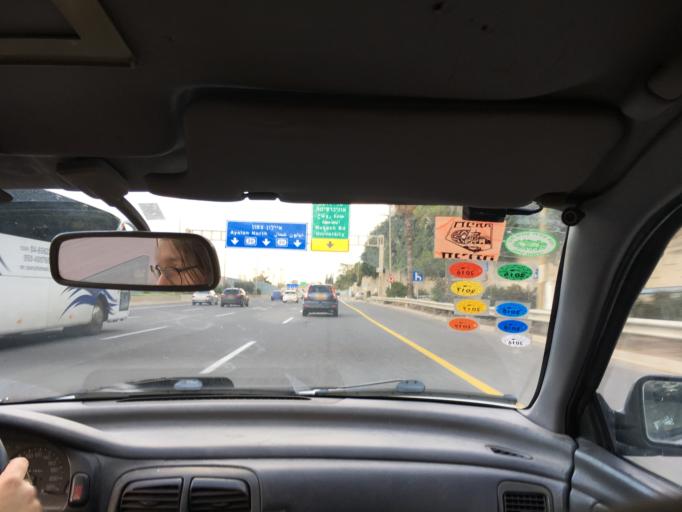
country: IL
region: Tel Aviv
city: Ramat Gan
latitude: 32.0906
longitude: 34.8011
